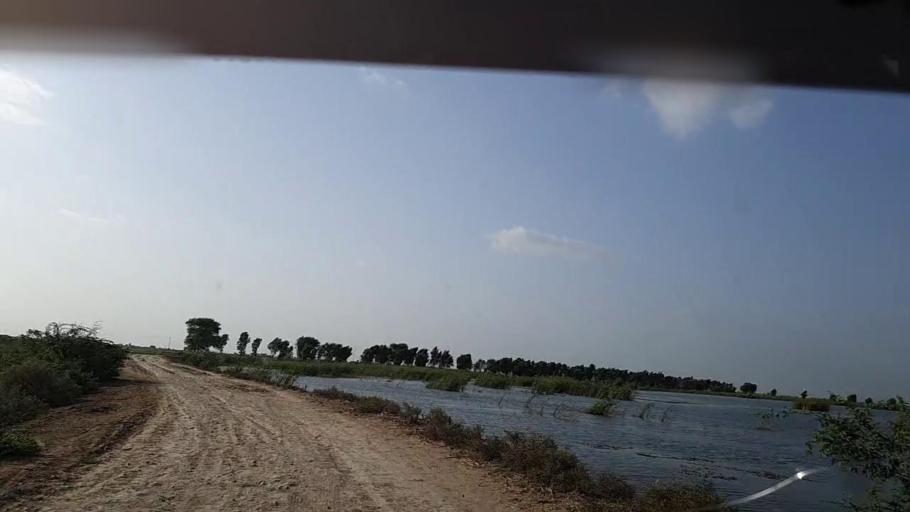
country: PK
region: Sindh
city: Badin
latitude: 24.5591
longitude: 68.8877
